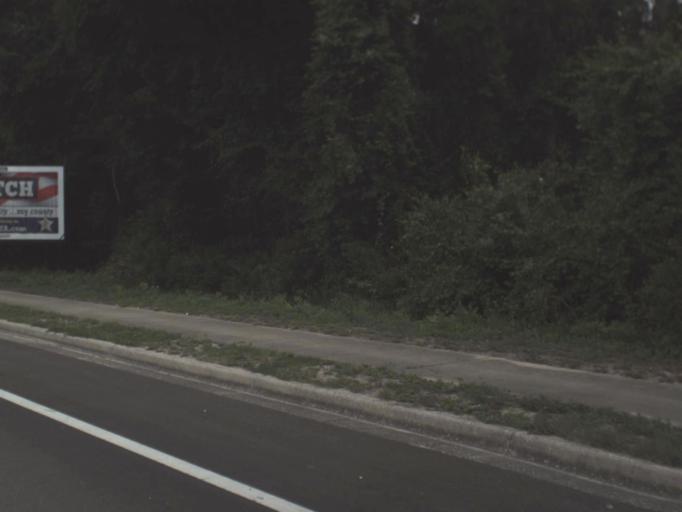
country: US
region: Florida
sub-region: Alachua County
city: Gainesville
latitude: 29.6433
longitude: -82.2901
